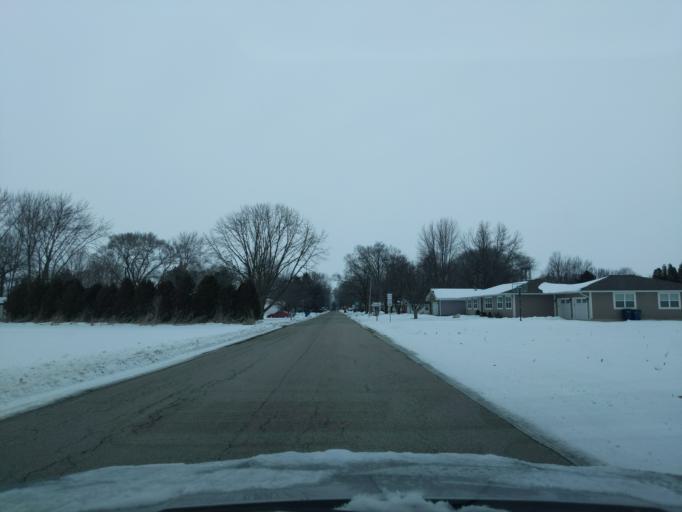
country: US
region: Indiana
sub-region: Benton County
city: Otterbein
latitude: 40.4807
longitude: -87.0939
